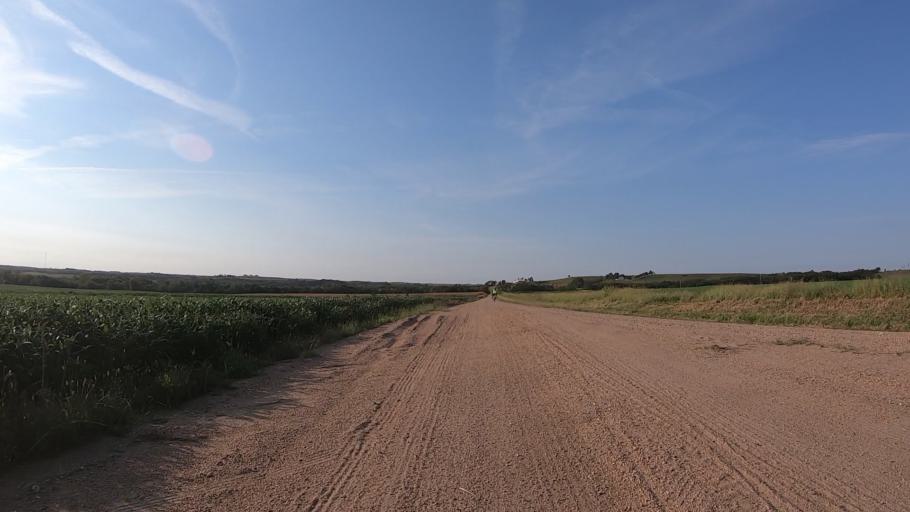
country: US
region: Kansas
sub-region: Marshall County
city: Blue Rapids
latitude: 39.6967
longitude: -96.7792
